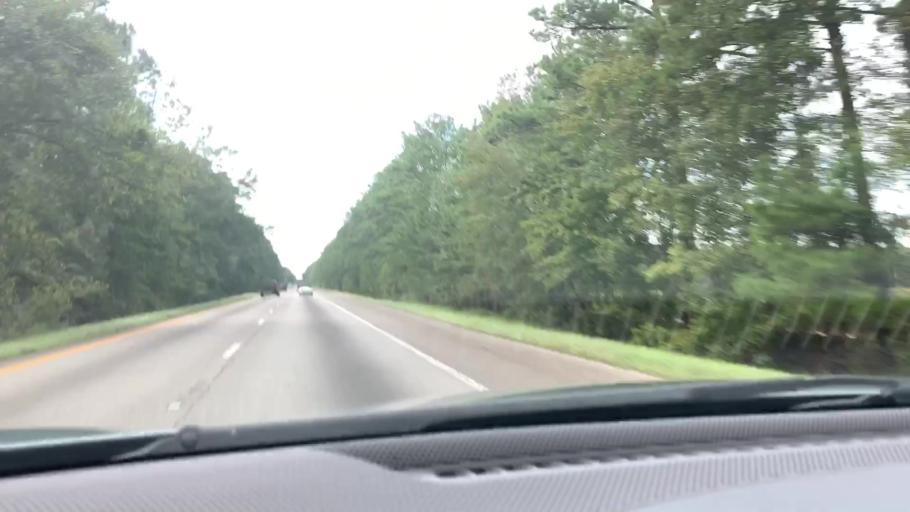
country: US
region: South Carolina
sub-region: Dorchester County
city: Saint George
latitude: 33.3371
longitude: -80.5672
